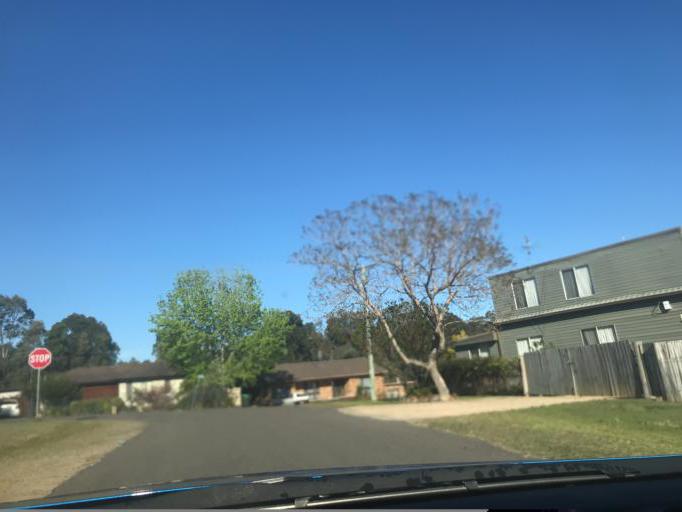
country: AU
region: New South Wales
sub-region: Cessnock
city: Cessnock
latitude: -32.9049
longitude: 151.2853
